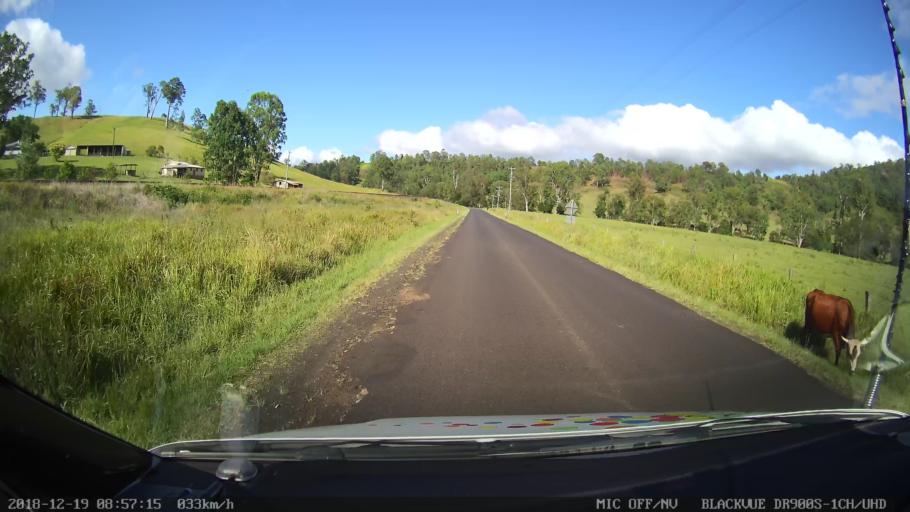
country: AU
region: New South Wales
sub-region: Kyogle
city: Kyogle
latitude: -28.4205
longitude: 152.9733
